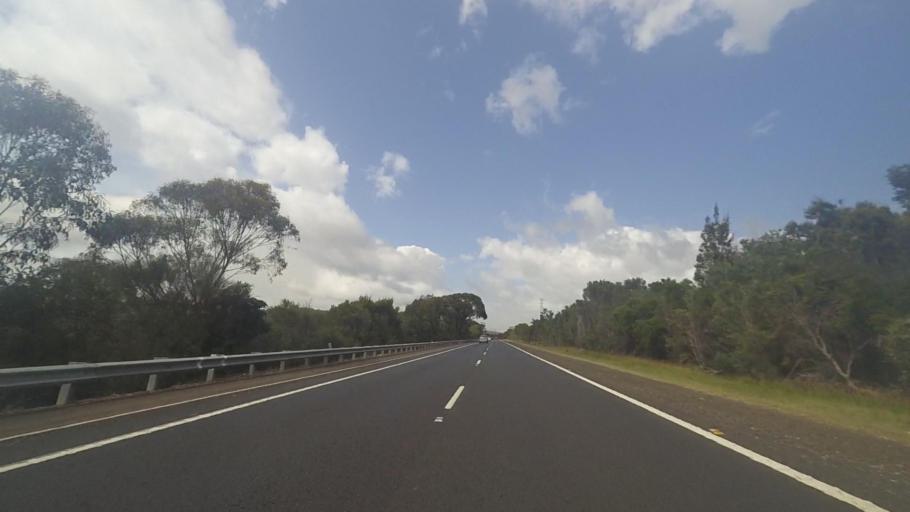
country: AU
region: New South Wales
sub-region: Wollongong
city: Helensburgh
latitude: -34.1845
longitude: 150.9710
